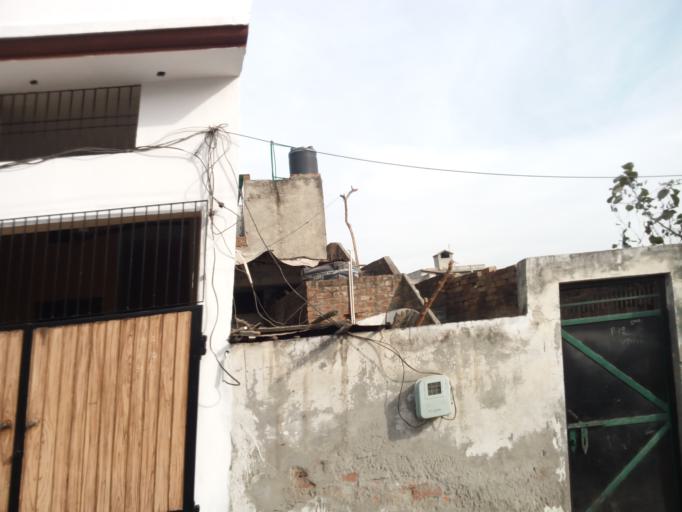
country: IN
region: Punjab
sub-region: Hoshiarpur
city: Hoshiarpur
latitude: 31.5247
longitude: 75.9027
